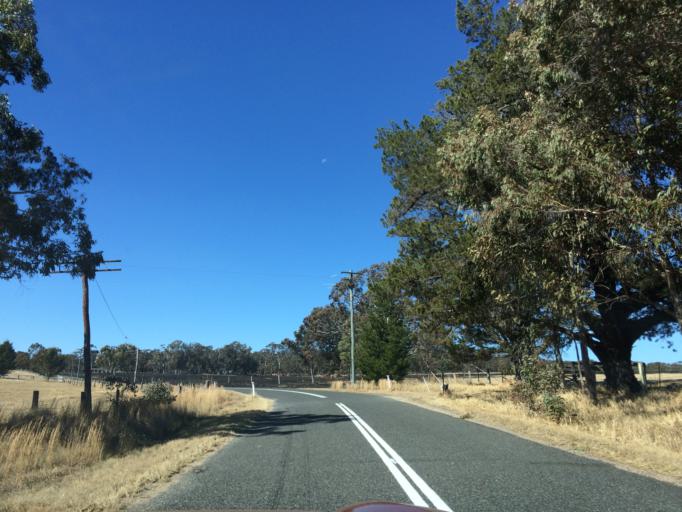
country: AU
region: Queensland
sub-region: Southern Downs
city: Stanthorpe
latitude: -28.6956
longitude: 152.0139
